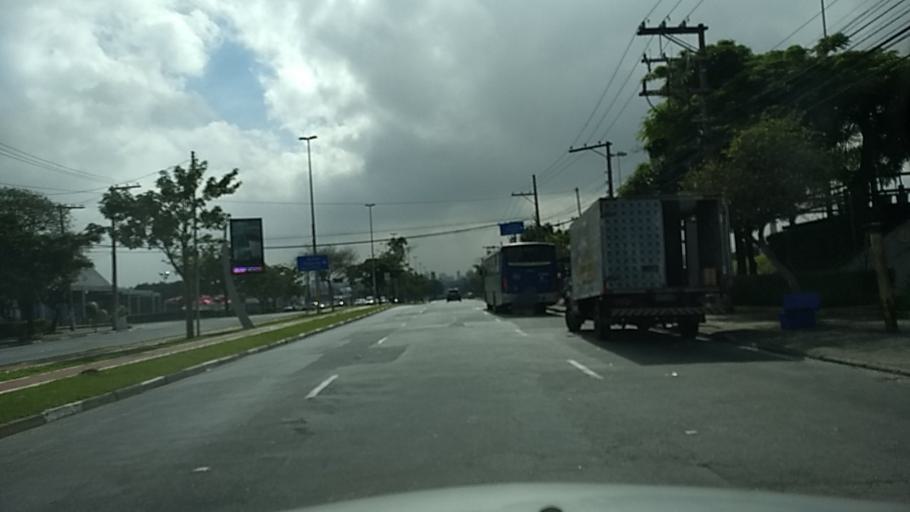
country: BR
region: Sao Paulo
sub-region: Sao Paulo
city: Sao Paulo
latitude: -23.5139
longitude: -46.6160
